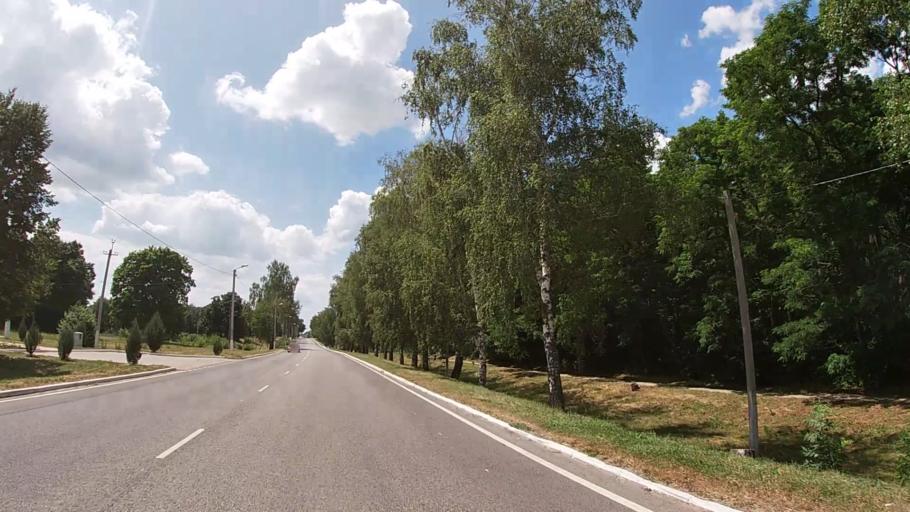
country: RU
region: Belgorod
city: Grayvoron
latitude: 50.4888
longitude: 35.6935
